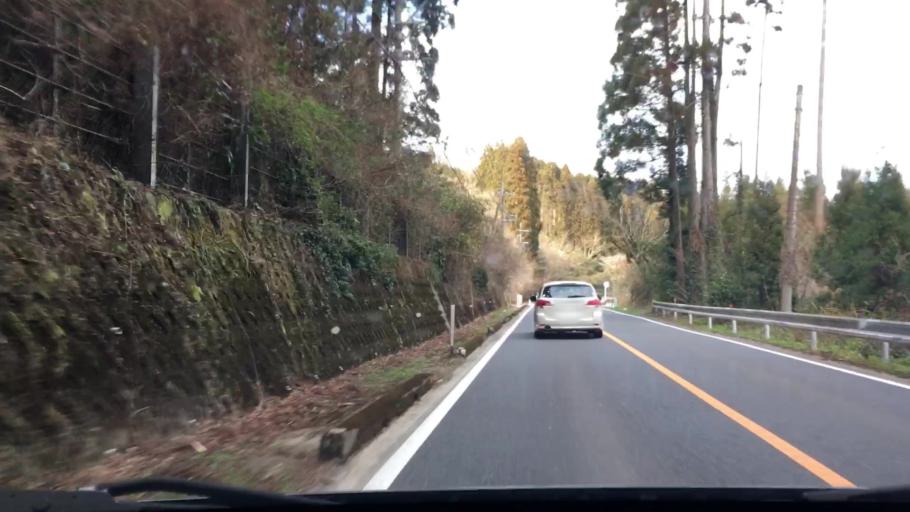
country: JP
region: Miyazaki
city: Nichinan
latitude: 31.7285
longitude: 131.3302
